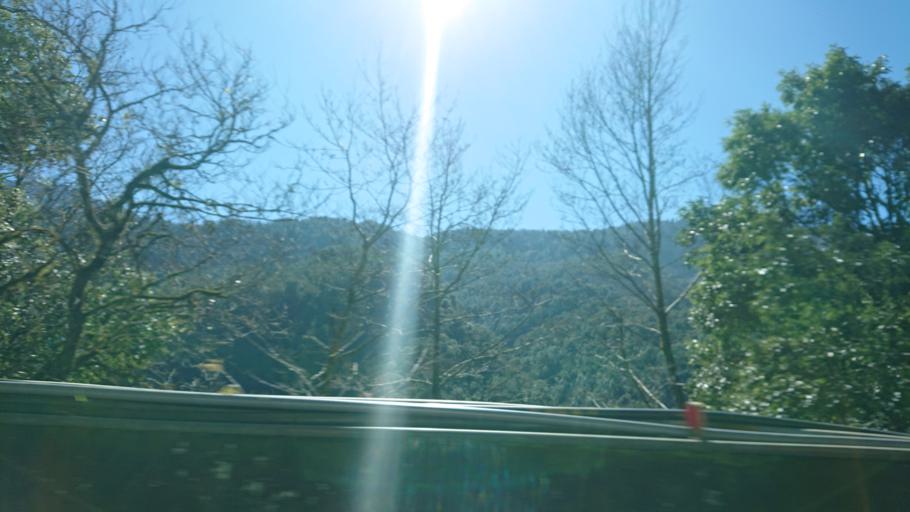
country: TW
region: Taiwan
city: Daxi
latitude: 24.4124
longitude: 121.3628
